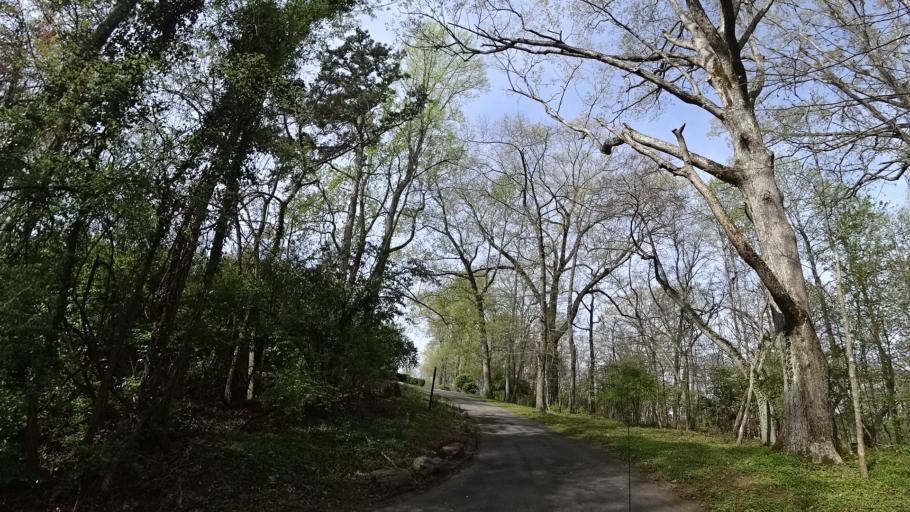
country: US
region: Tennessee
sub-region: Knox County
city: Knoxville
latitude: 35.9033
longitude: -83.9856
